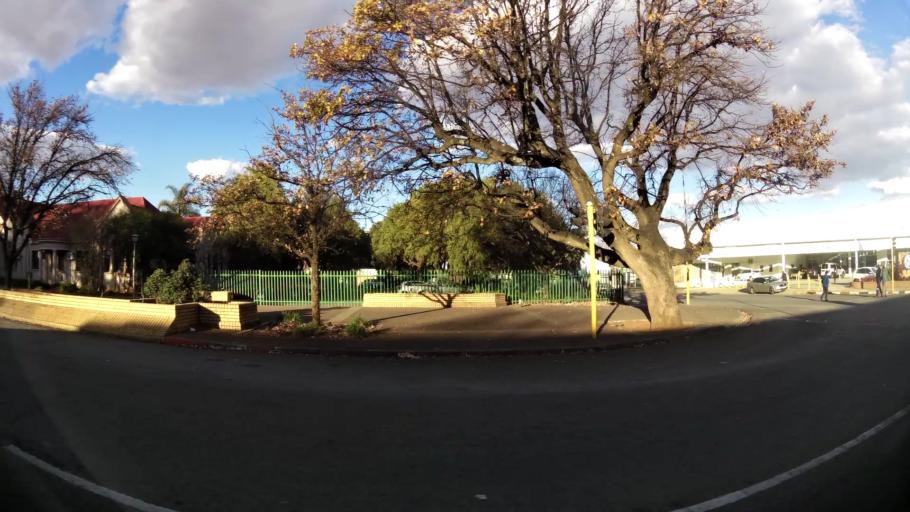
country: ZA
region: North-West
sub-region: Dr Kenneth Kaunda District Municipality
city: Potchefstroom
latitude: -26.7161
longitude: 27.0969
